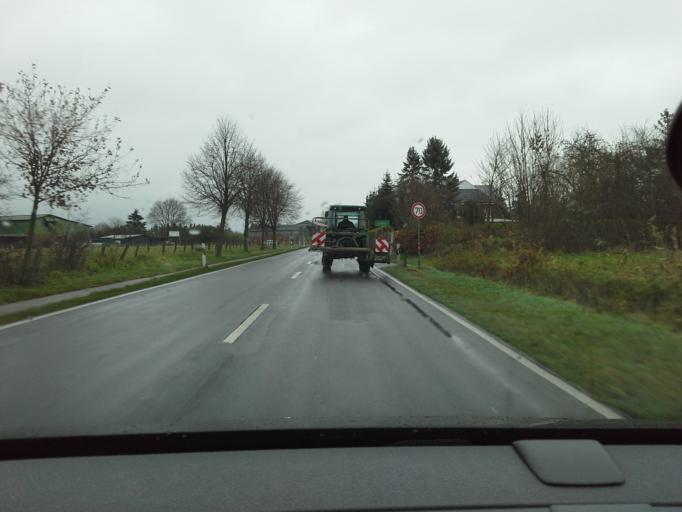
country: DE
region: Schleswig-Holstein
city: Bevern
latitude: 53.7472
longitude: 9.7964
